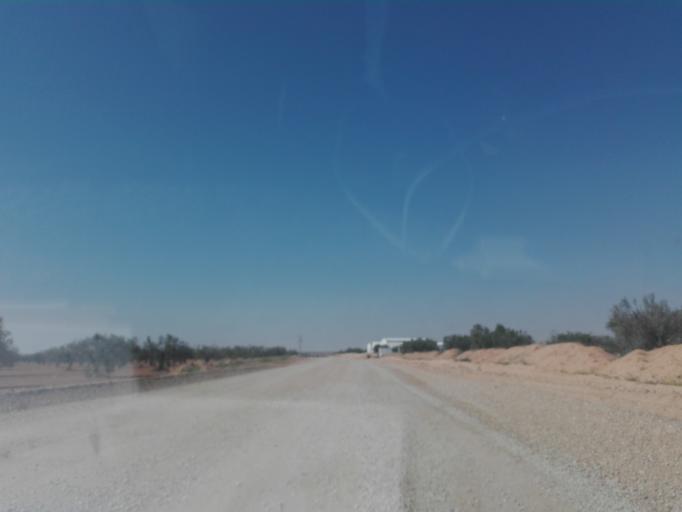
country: TN
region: Safaqis
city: Sfax
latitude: 34.7015
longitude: 10.4852
